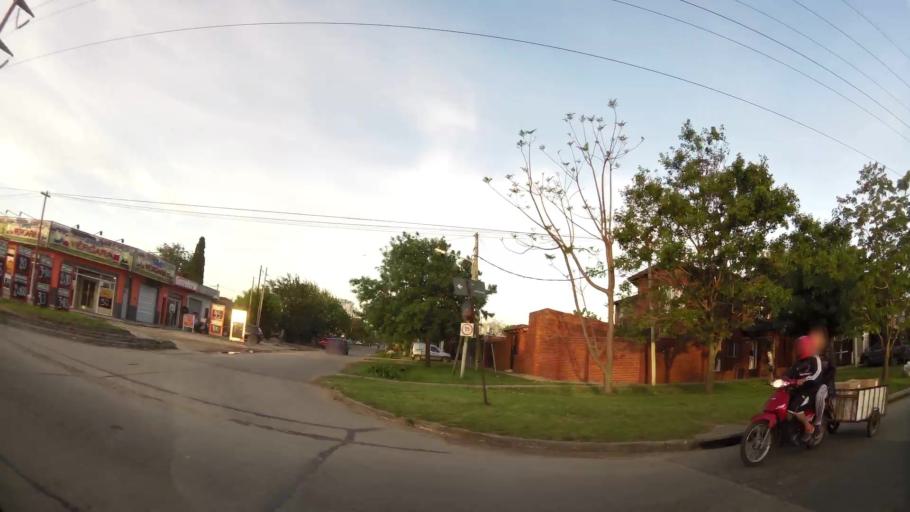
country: AR
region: Buenos Aires
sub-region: Partido de Quilmes
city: Quilmes
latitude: -34.7758
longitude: -58.2281
